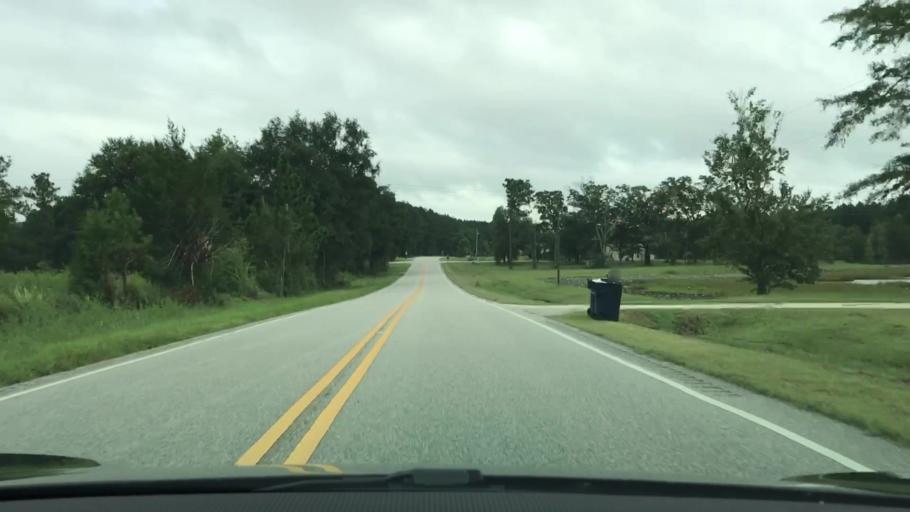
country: US
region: Alabama
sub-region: Geneva County
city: Samson
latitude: 31.0158
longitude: -86.1256
